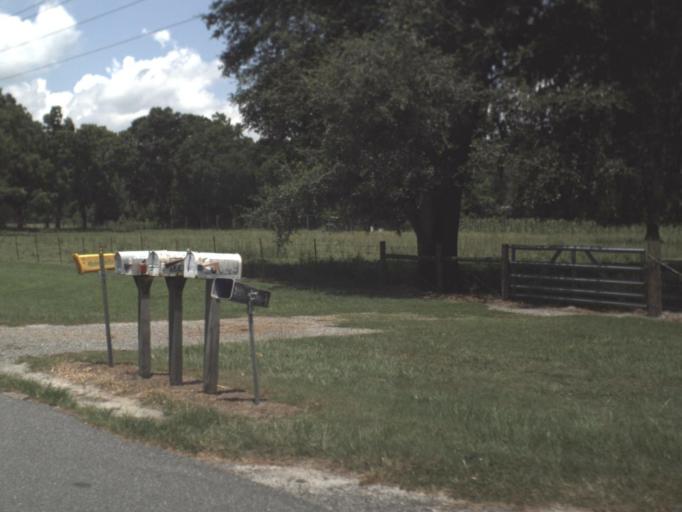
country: US
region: Florida
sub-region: Alachua County
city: High Springs
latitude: 30.0032
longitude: -82.5351
